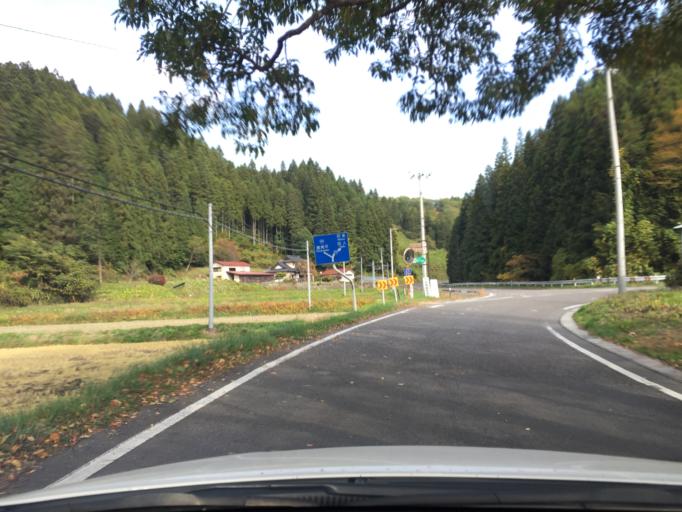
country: JP
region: Fukushima
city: Ishikawa
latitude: 36.9910
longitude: 140.4994
